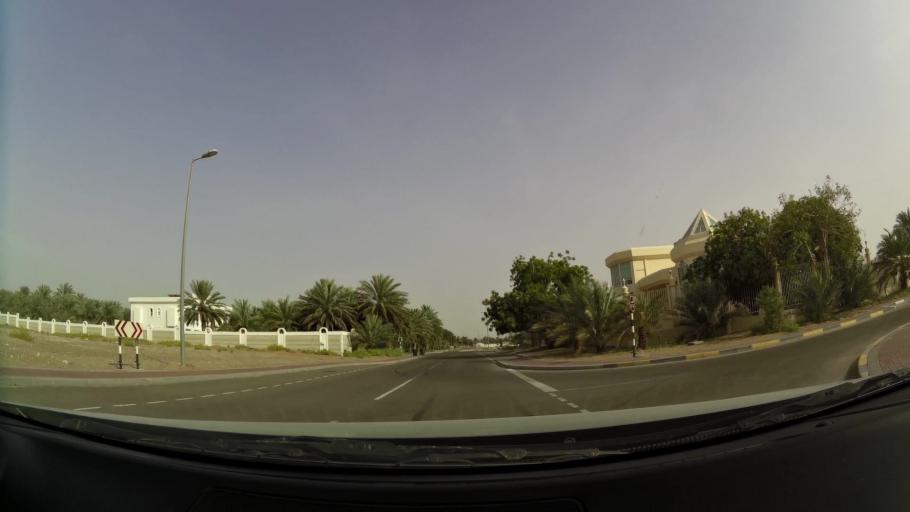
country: AE
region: Abu Dhabi
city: Al Ain
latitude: 24.1959
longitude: 55.6127
